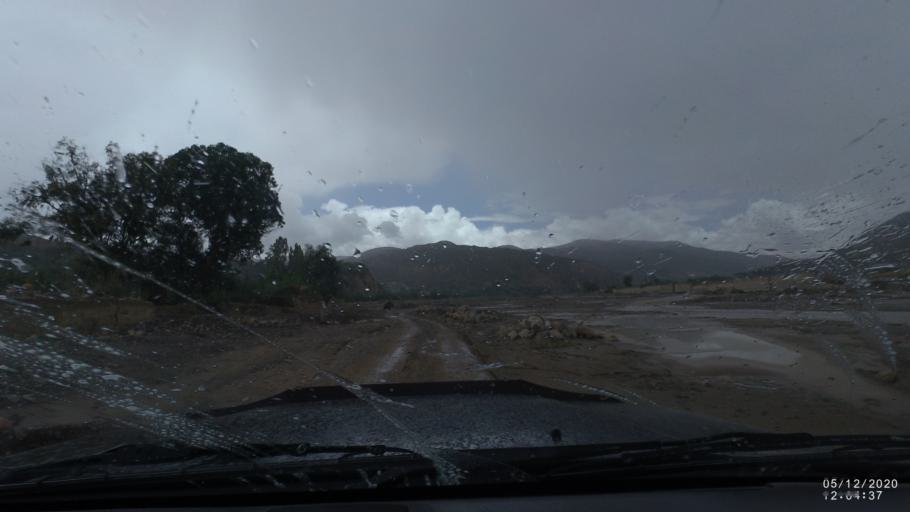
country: BO
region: Cochabamba
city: Sipe Sipe
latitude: -17.5718
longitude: -66.3574
